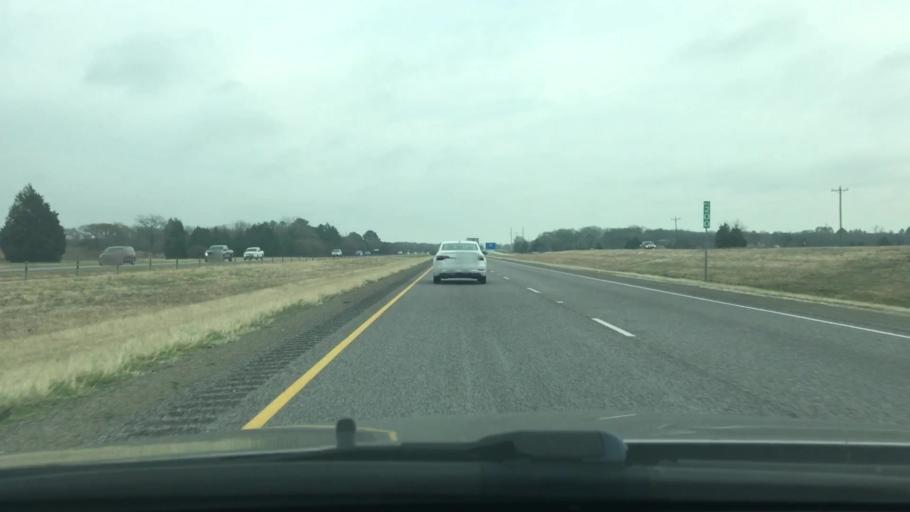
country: US
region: Texas
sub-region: Freestone County
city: Fairfield
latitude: 31.7405
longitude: -96.1907
